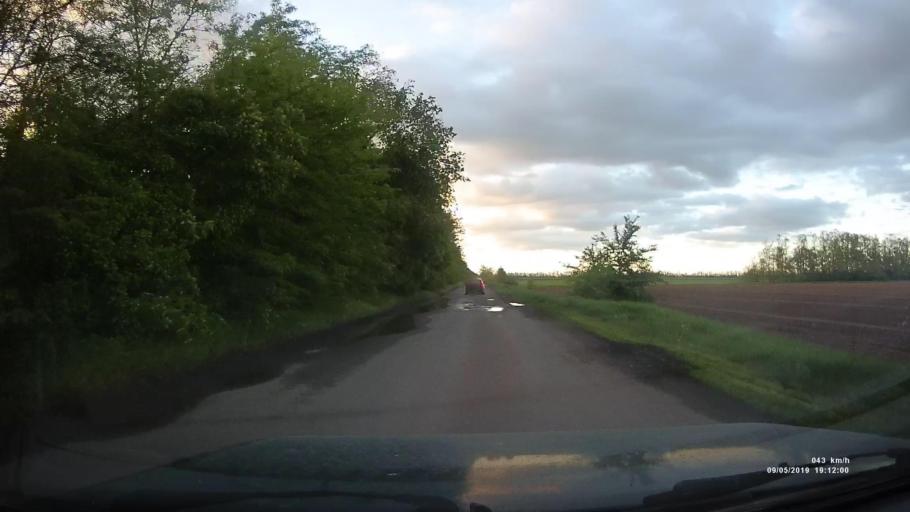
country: RU
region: Krasnodarskiy
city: Kanelovskaya
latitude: 46.7388
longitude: 39.2136
